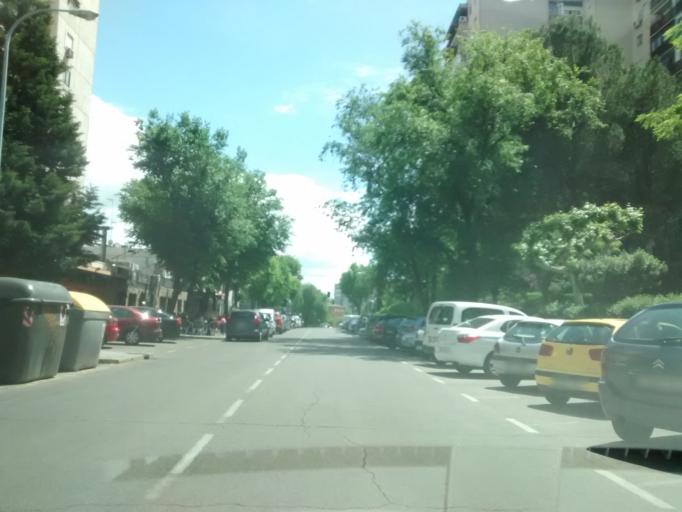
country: ES
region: Madrid
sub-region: Provincia de Madrid
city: San Fernando de Henares
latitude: 40.4265
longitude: -3.5399
